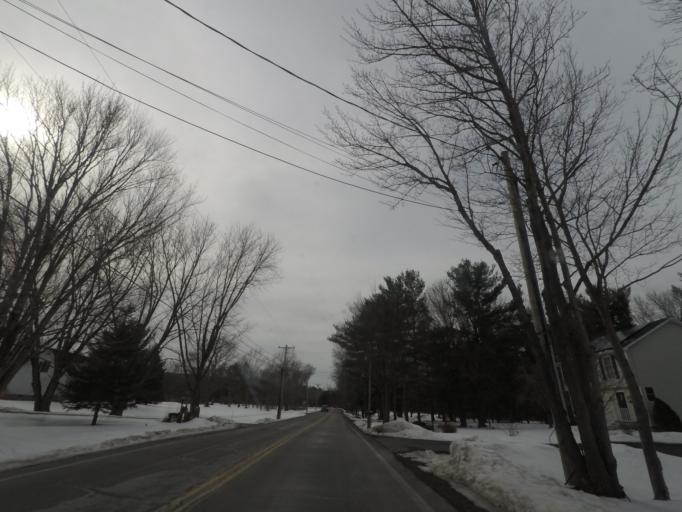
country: US
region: New York
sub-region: Albany County
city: Altamont
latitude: 42.6969
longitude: -73.9751
